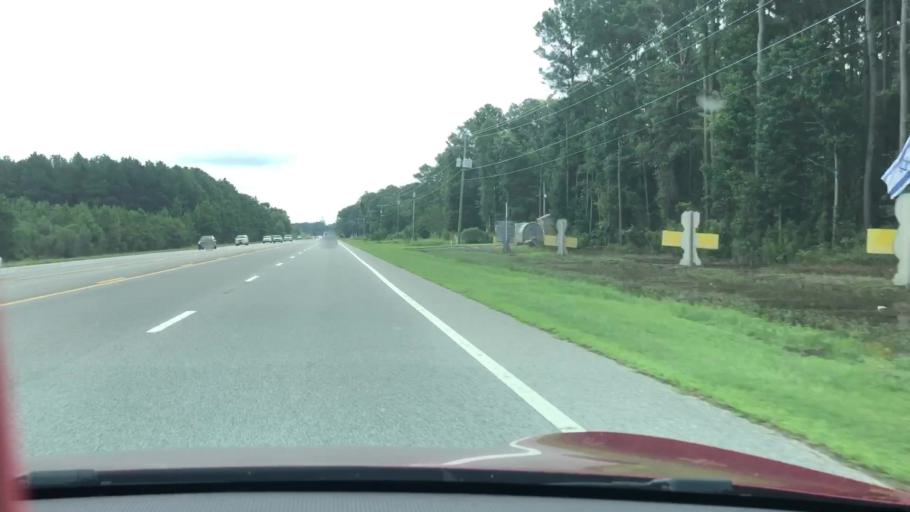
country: US
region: North Carolina
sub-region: Currituck County
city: Currituck
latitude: 36.4544
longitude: -76.0501
